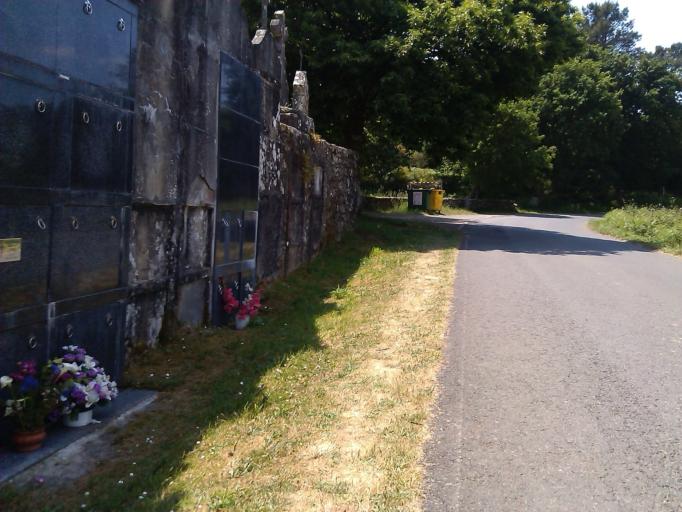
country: ES
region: Galicia
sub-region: Provincia de Lugo
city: Monterroso
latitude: 42.8733
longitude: -7.8166
